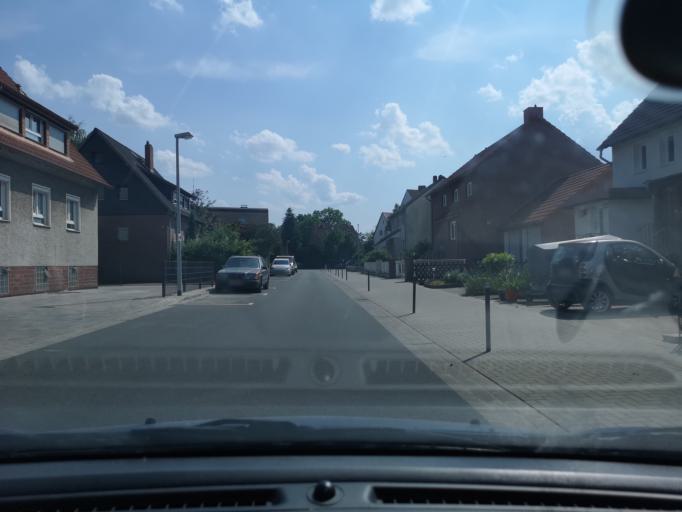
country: DE
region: Lower Saxony
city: Langenhagen
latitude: 52.4332
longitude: 9.7377
